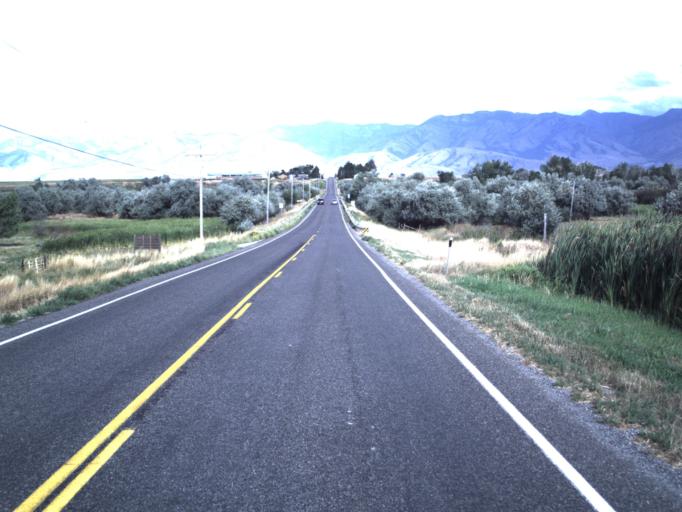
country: US
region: Utah
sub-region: Cache County
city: Lewiston
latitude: 41.9754
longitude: -111.9418
